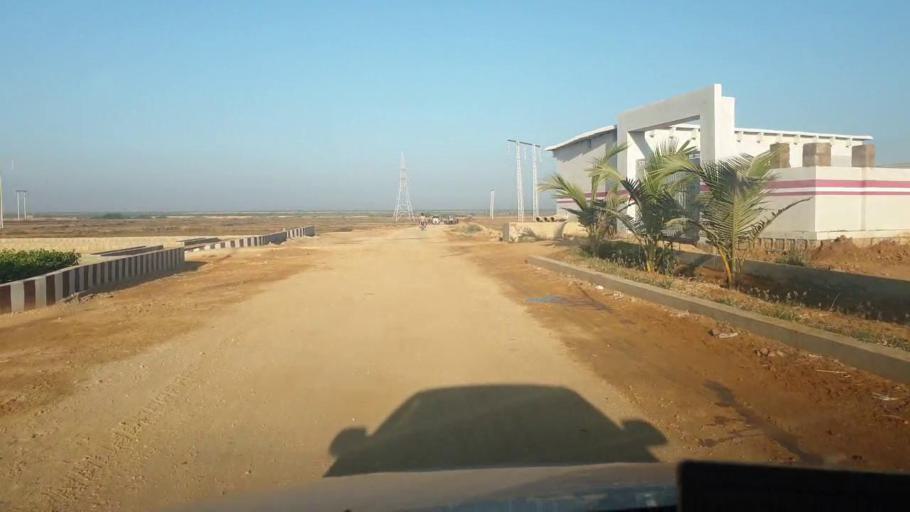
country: PK
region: Sindh
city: Thatta
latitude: 24.6995
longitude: 67.8559
